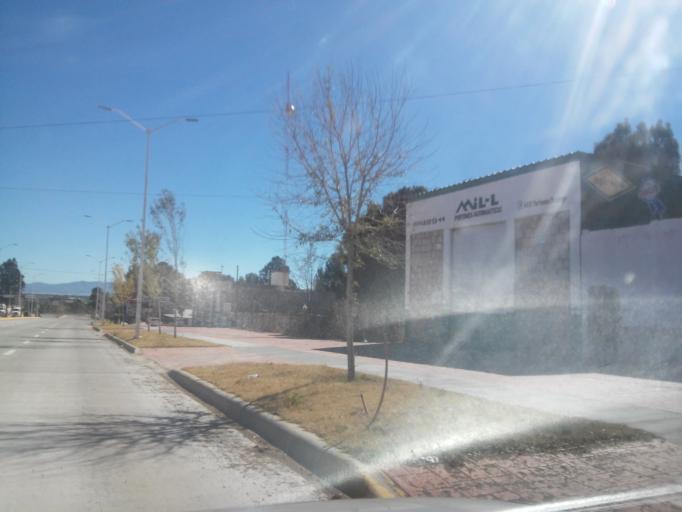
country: MX
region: Durango
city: Victoria de Durango
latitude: 23.9931
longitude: -104.7135
